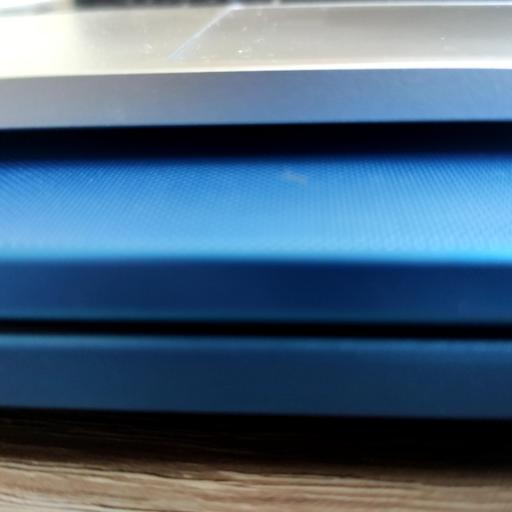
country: RU
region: Moskovskaya
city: Levoberezhnaya
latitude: 55.8996
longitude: 37.4613
